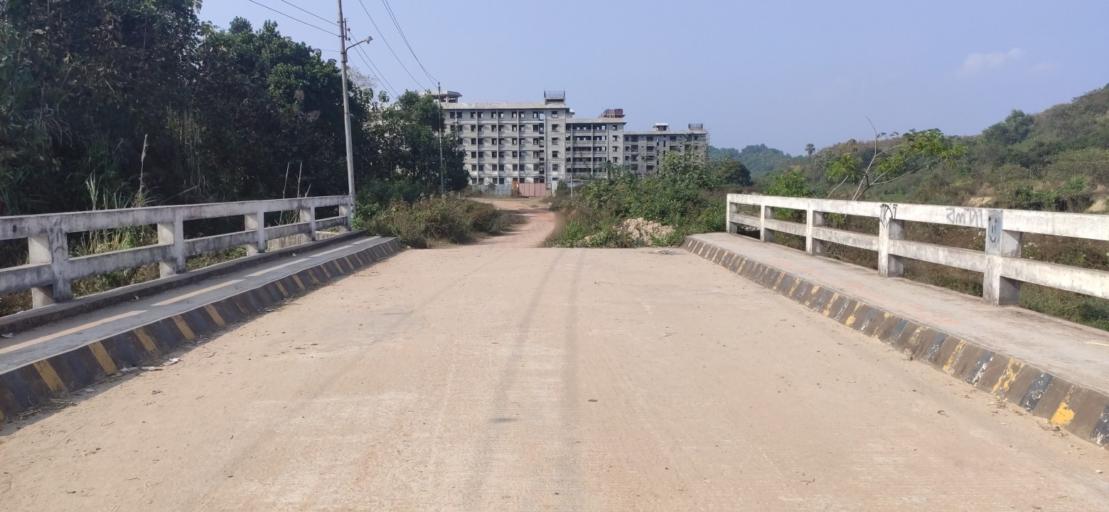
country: BD
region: Chittagong
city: Chittagong
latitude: 22.4753
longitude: 91.7845
